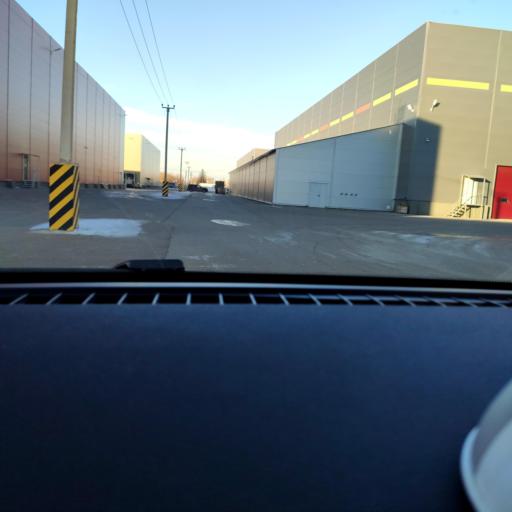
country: RU
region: Samara
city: Samara
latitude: 53.0945
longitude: 50.1297
